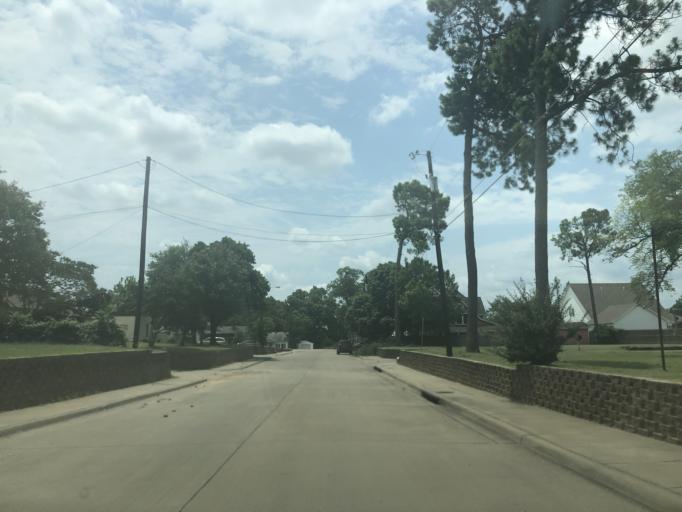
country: US
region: Texas
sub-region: Dallas County
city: Irving
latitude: 32.7951
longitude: -96.9325
